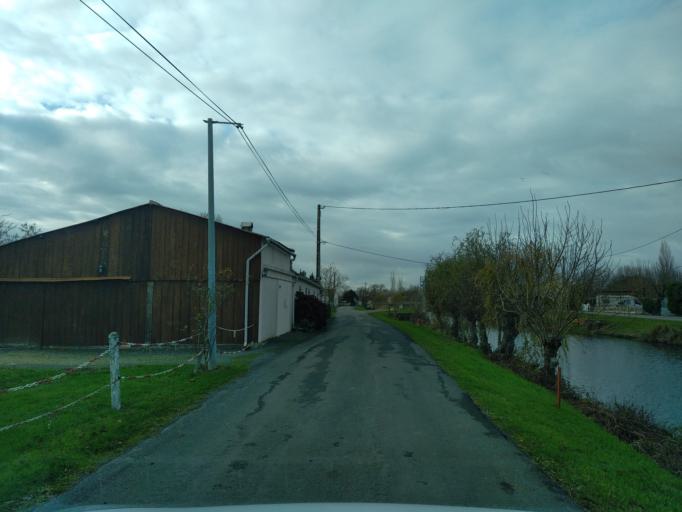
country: FR
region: Pays de la Loire
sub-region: Departement de la Vendee
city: Maillezais
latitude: 46.3183
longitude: -0.7730
